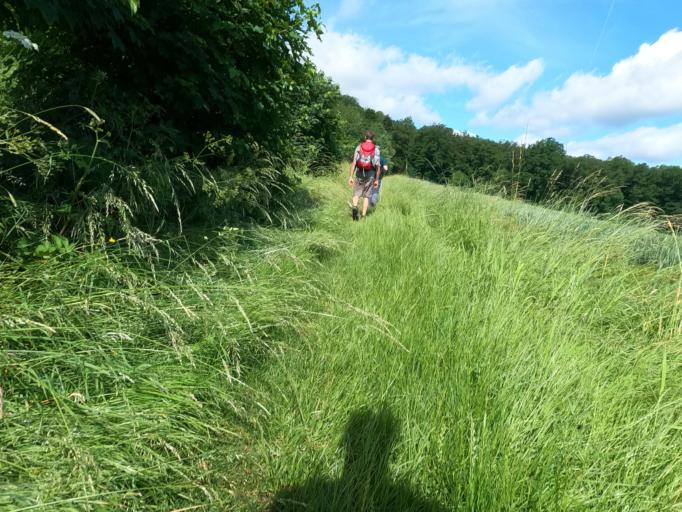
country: DE
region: Rheinland-Pfalz
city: Hachenburg
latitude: 50.6745
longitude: 7.8081
